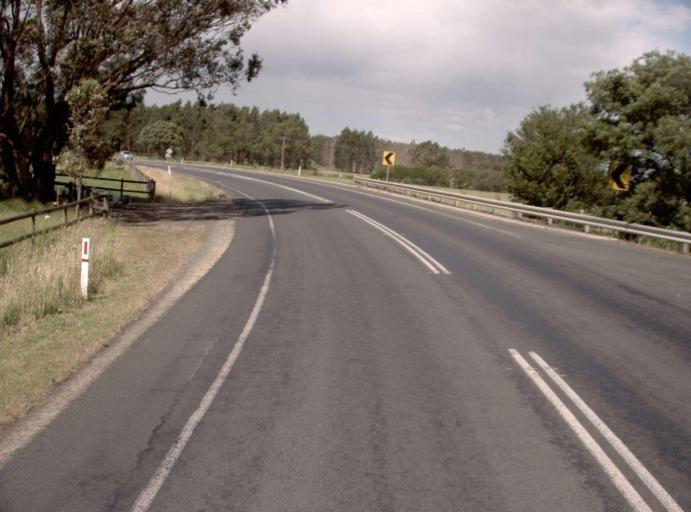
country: AU
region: Victoria
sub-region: Latrobe
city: Morwell
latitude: -38.1625
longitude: 146.4042
